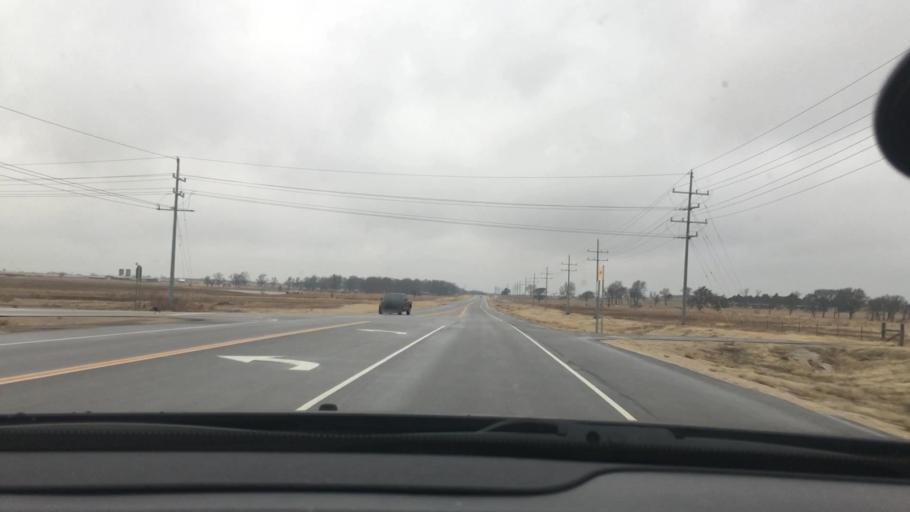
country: US
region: Oklahoma
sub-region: Johnston County
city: Tishomingo
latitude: 34.3618
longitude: -96.6361
